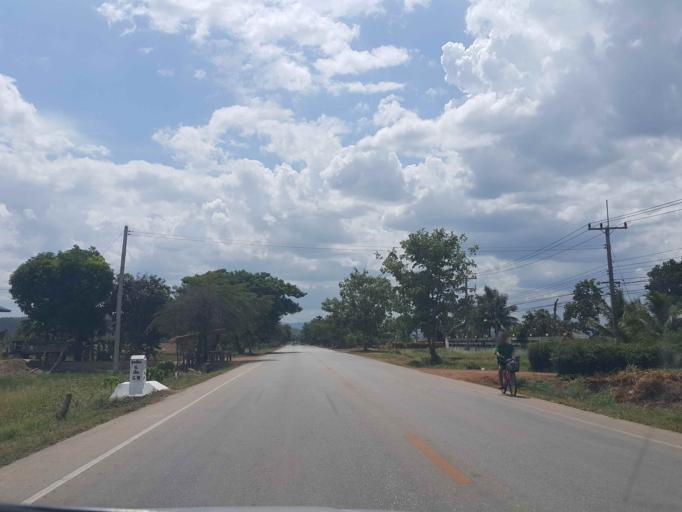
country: TH
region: Sukhothai
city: Thung Saliam
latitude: 17.3355
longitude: 99.6143
